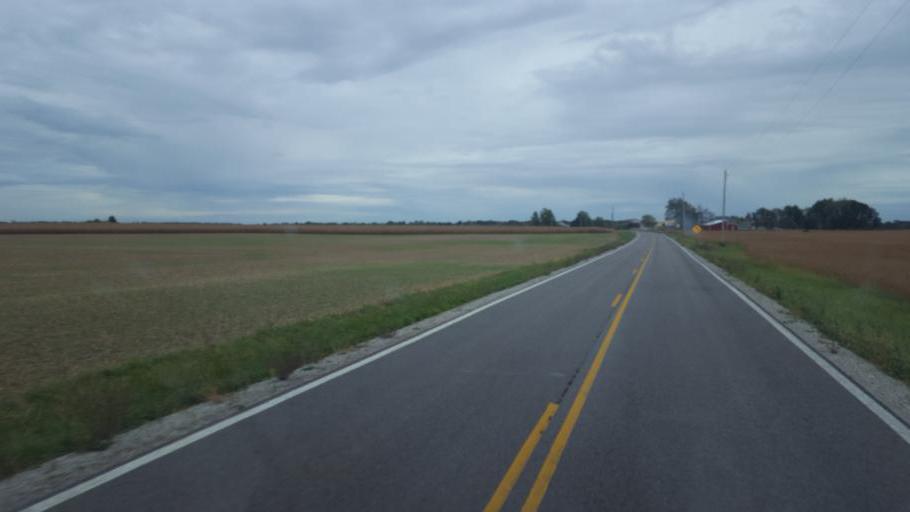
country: US
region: Ohio
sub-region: Huron County
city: New London
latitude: 41.1430
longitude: -82.4252
